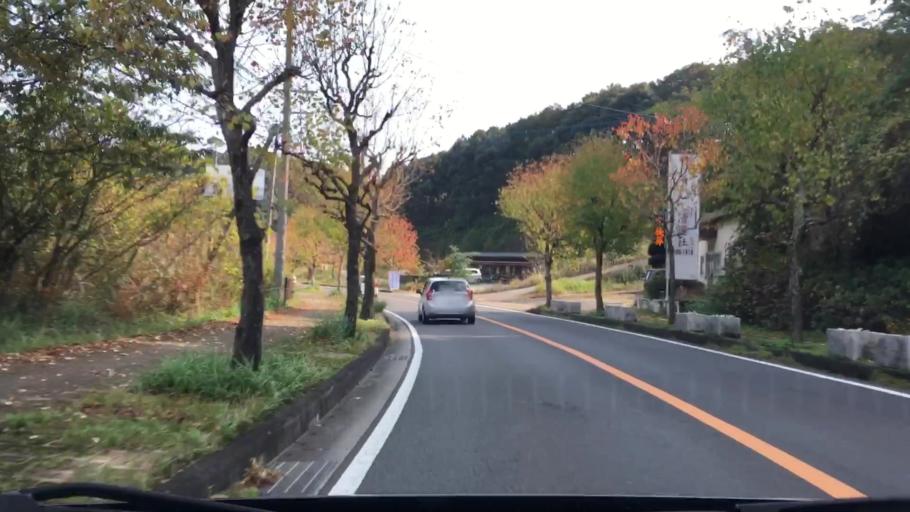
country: JP
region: Nagasaki
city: Togitsu
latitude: 32.9868
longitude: 129.7679
